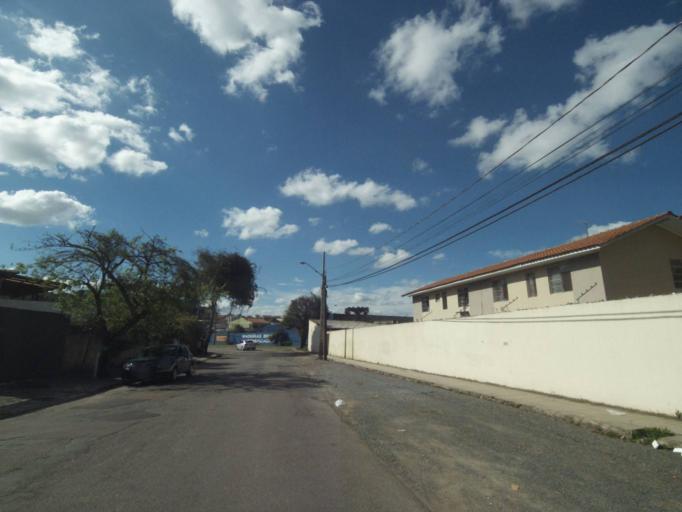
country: BR
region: Parana
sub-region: Curitiba
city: Curitiba
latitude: -25.3811
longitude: -49.2495
